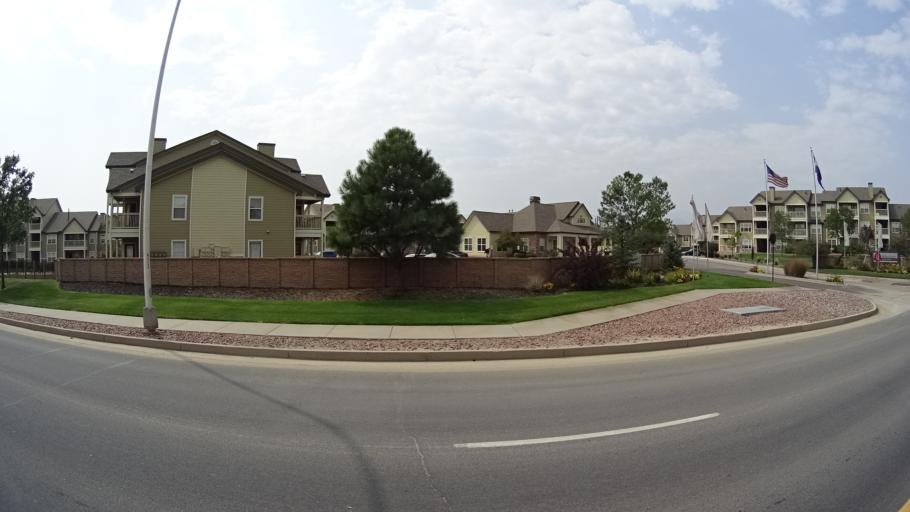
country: US
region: Colorado
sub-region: El Paso County
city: Stratmoor
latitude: 38.8177
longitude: -104.7463
